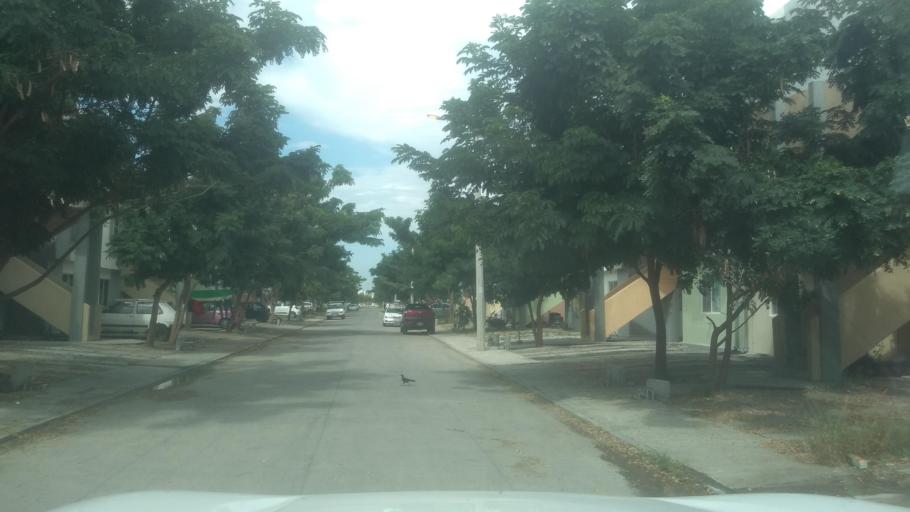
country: MX
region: Veracruz
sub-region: Medellin
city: Fraccionamiento Arboledas San Ramon
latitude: 19.0923
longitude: -96.1671
